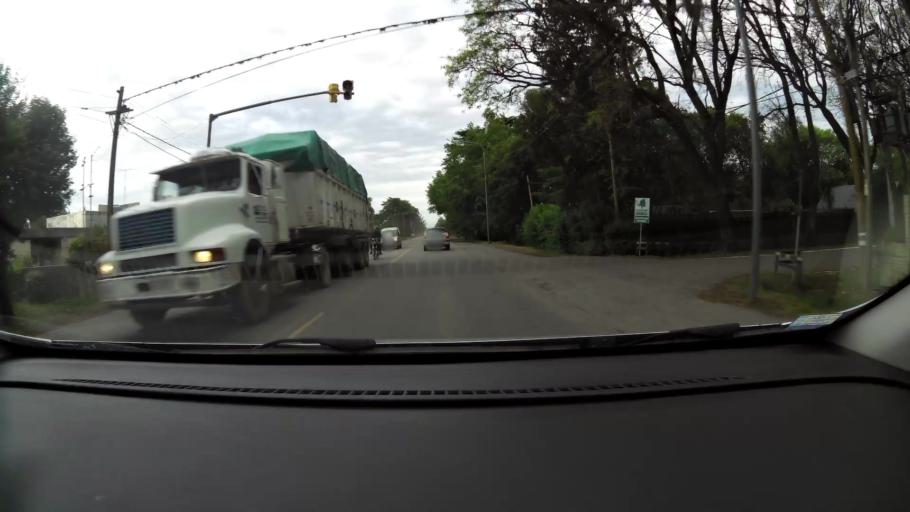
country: AR
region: Buenos Aires
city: San Nicolas de los Arroyos
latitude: -33.3789
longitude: -60.2099
